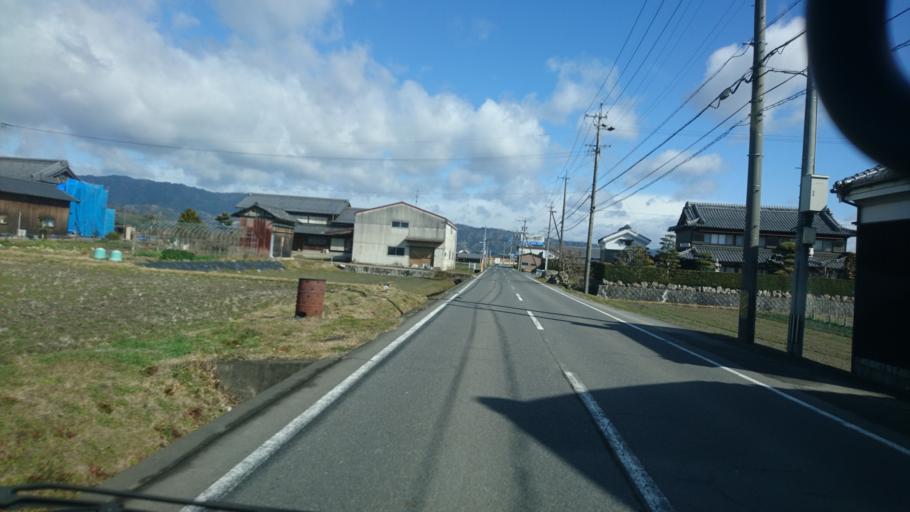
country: JP
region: Mie
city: Ueno-ebisumachi
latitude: 34.7565
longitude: 136.1114
